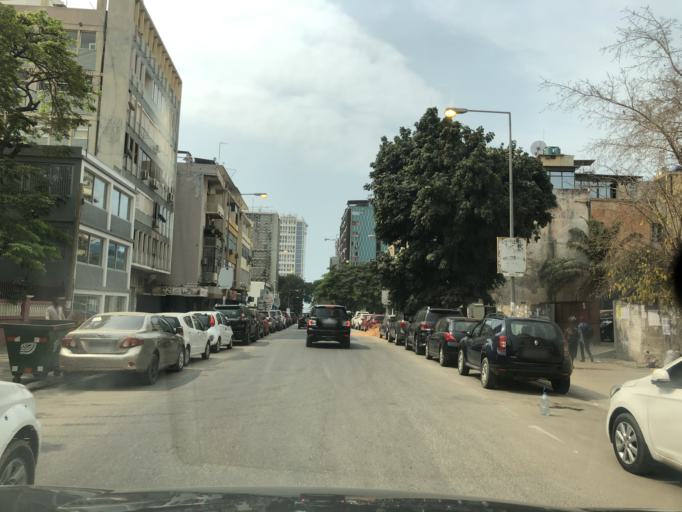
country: AO
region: Luanda
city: Luanda
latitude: -8.8174
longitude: 13.2318
